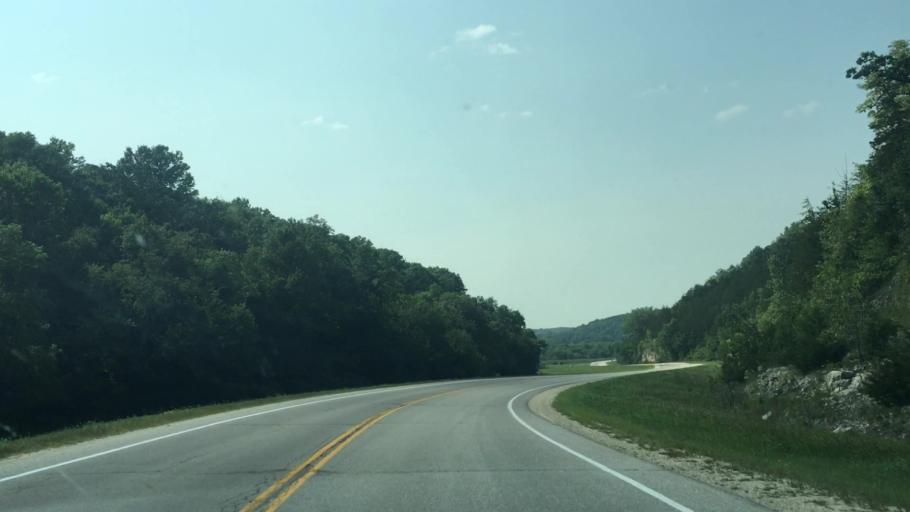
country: US
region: Minnesota
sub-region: Fillmore County
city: Preston
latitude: 43.7067
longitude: -91.9728
